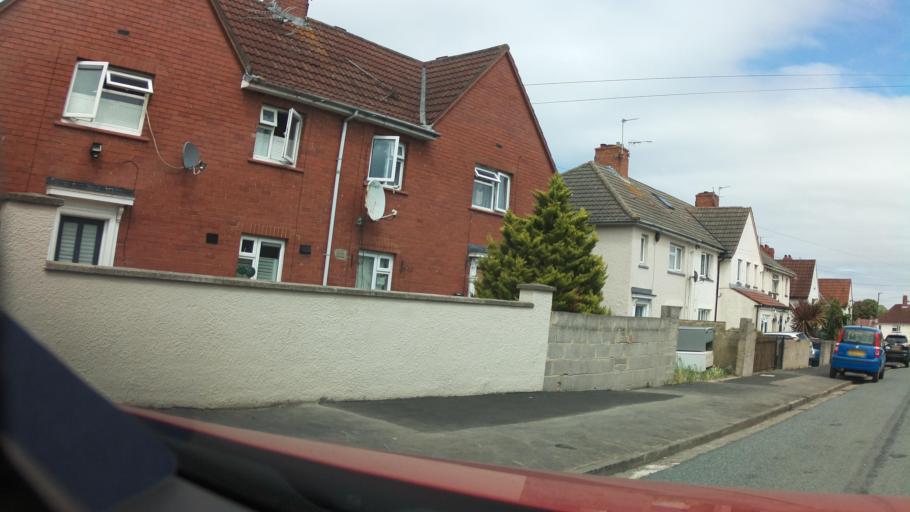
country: GB
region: England
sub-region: Bristol
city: Bristol
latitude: 51.4296
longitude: -2.5872
